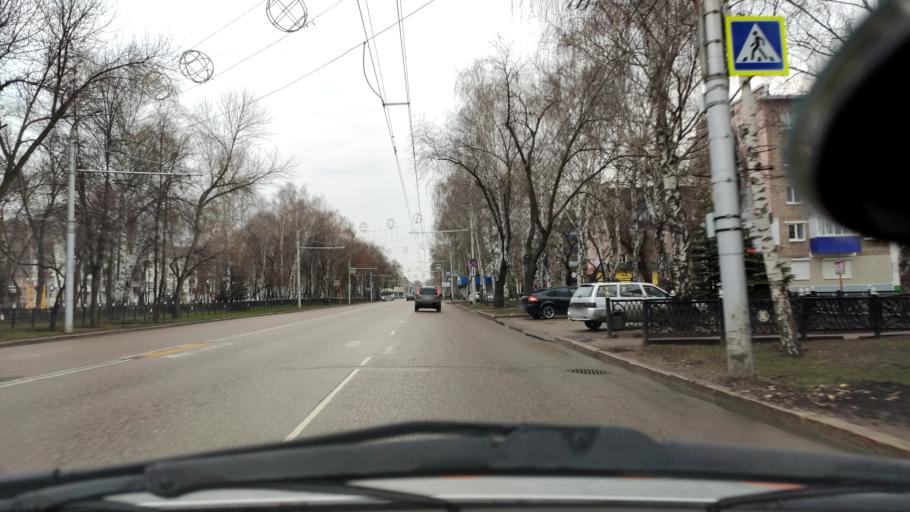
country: RU
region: Bashkortostan
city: Sterlitamak
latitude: 53.6337
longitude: 55.9340
